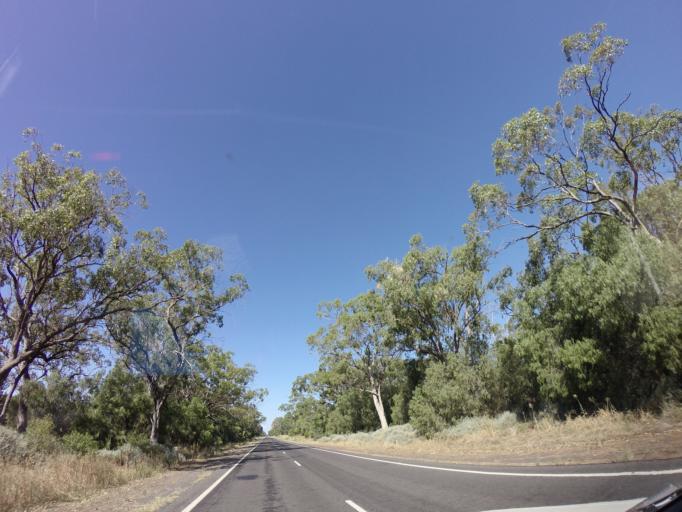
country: AU
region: New South Wales
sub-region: Narromine
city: Narromine
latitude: -31.6559
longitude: 147.8772
